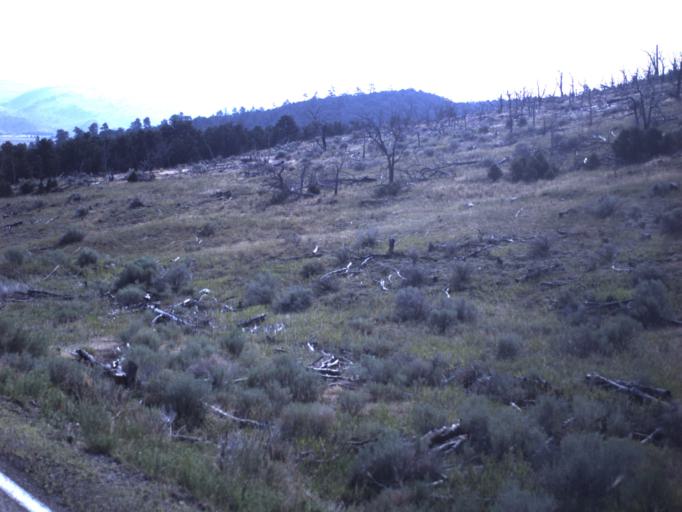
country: US
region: Utah
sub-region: Daggett County
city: Manila
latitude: 40.9290
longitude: -109.4132
